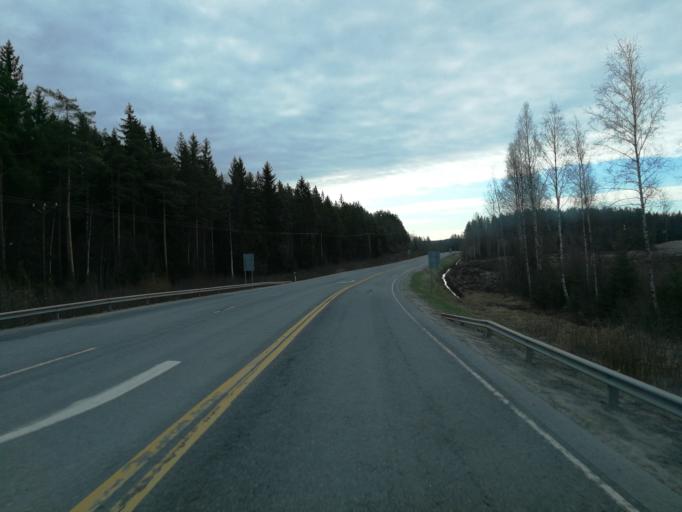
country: FI
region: Varsinais-Suomi
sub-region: Salo
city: Muurla
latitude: 60.3830
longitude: 23.2374
